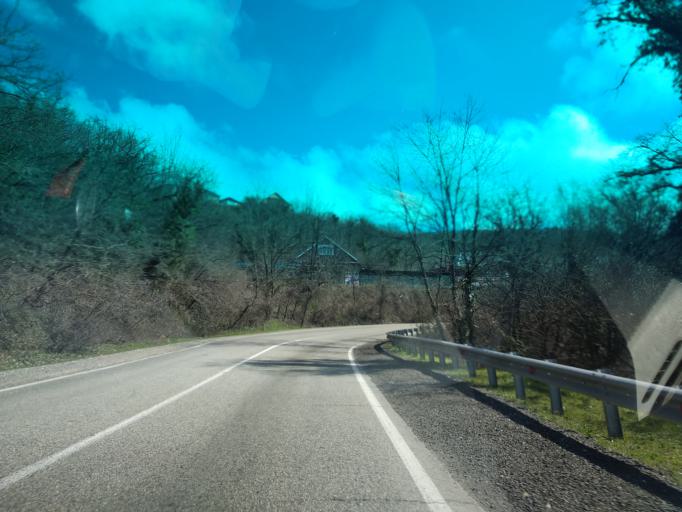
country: RU
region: Krasnodarskiy
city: Tuapse
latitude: 44.0902
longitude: 39.1216
